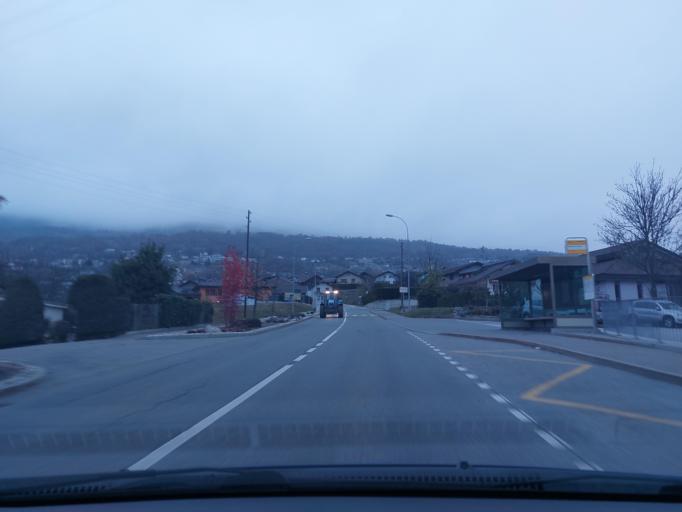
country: CH
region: Valais
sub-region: Sion District
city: Saviese
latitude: 46.2441
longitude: 7.3478
